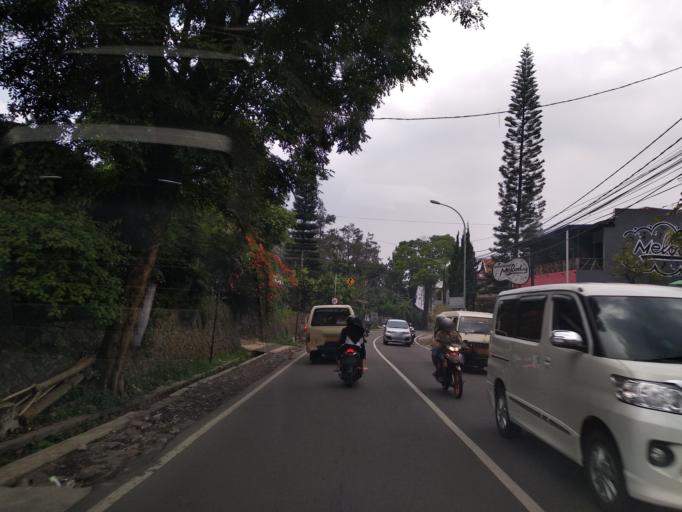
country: ID
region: West Java
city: Lembang
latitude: -6.8337
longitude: 107.6041
